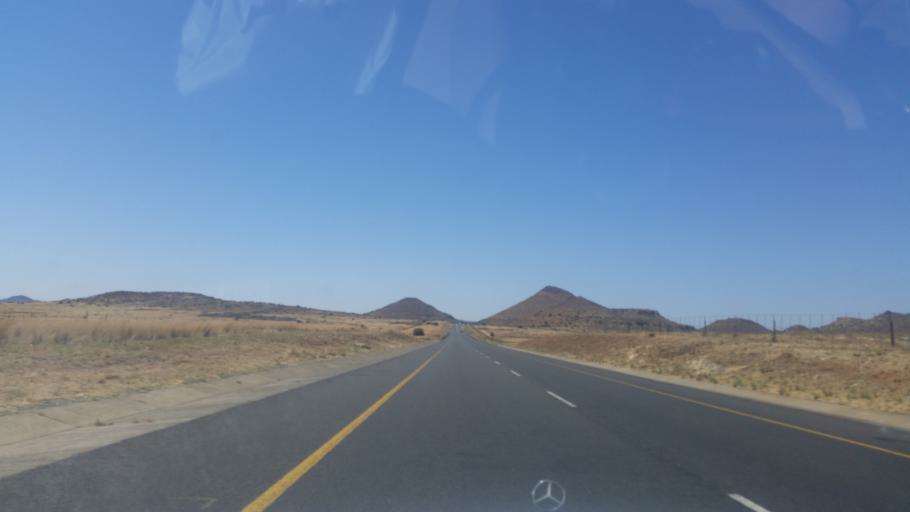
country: ZA
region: Northern Cape
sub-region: Pixley ka Seme District Municipality
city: Colesberg
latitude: -30.6064
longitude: 25.3874
